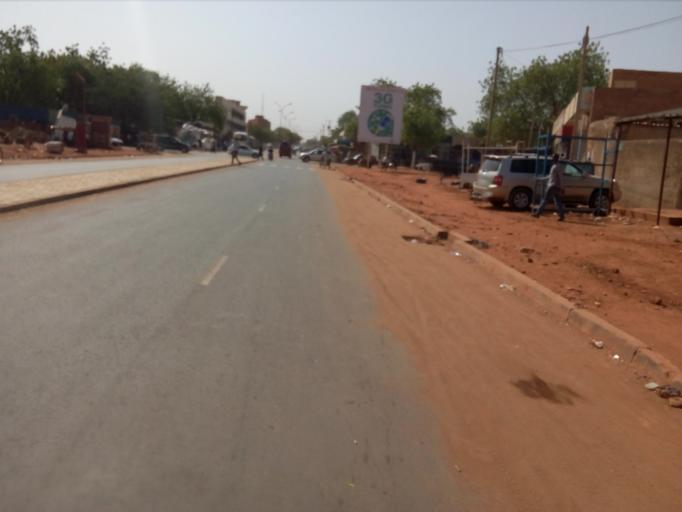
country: NE
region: Niamey
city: Niamey
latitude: 13.5200
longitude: 2.1224
